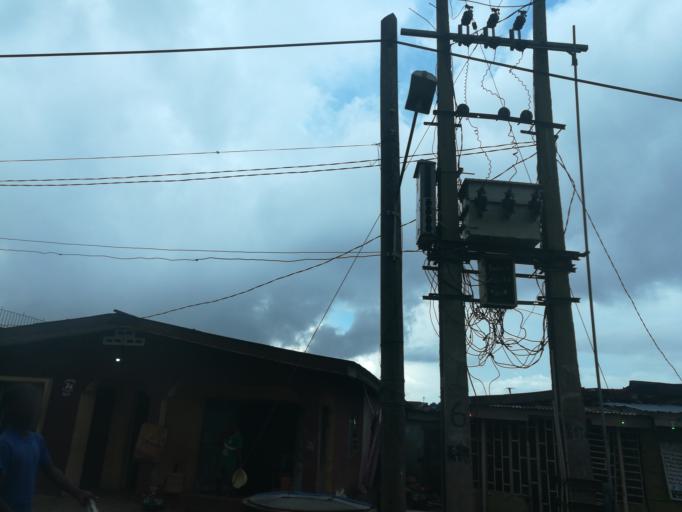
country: NG
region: Lagos
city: Agege
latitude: 6.6115
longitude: 3.3270
